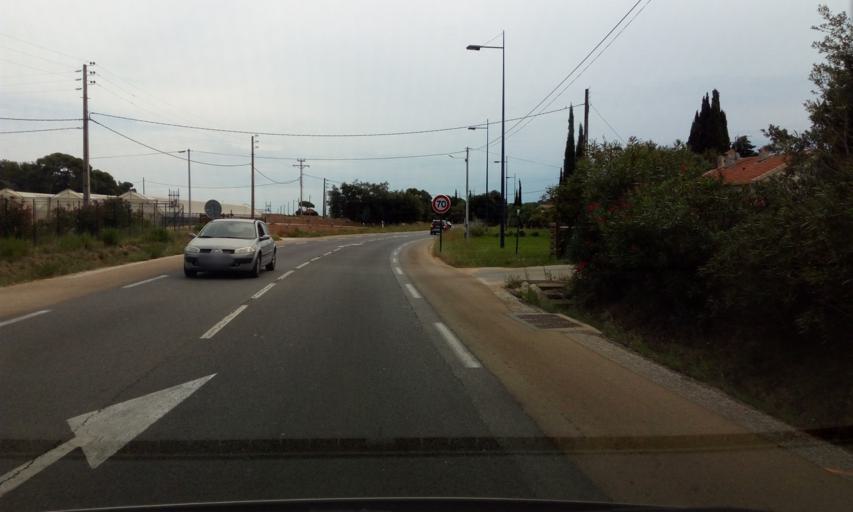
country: FR
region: Provence-Alpes-Cote d'Azur
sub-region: Departement du Var
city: Carqueiranne
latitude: 43.1032
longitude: 6.0558
